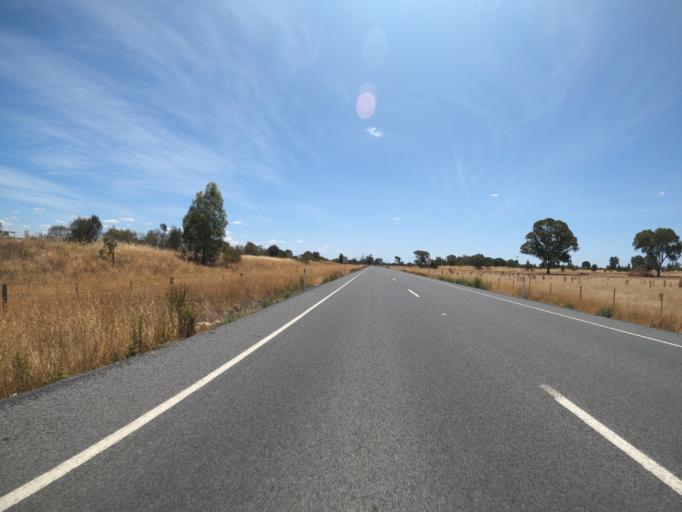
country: AU
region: Victoria
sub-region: Benalla
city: Benalla
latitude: -36.5192
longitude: 146.0340
